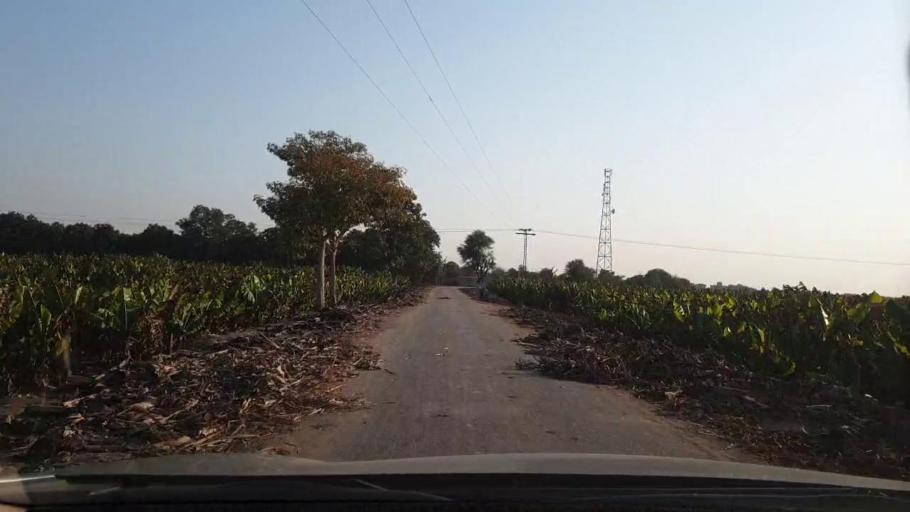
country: PK
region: Sindh
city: Berani
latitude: 25.6410
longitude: 68.8084
